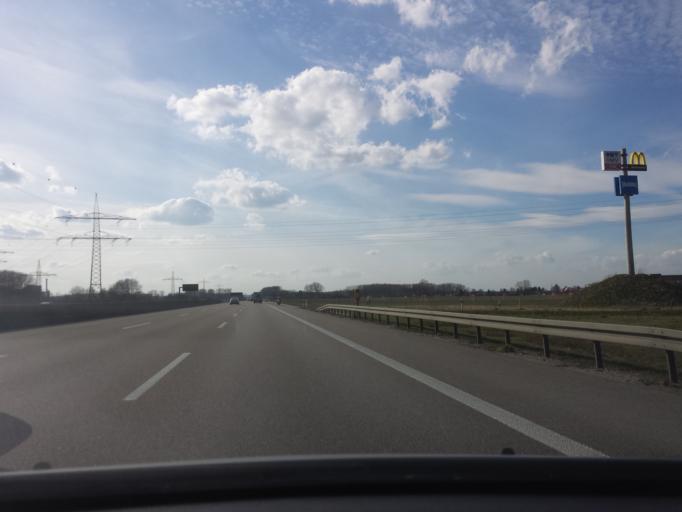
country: DE
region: Bavaria
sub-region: Swabia
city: Friedberg
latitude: 48.4046
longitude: 10.9526
